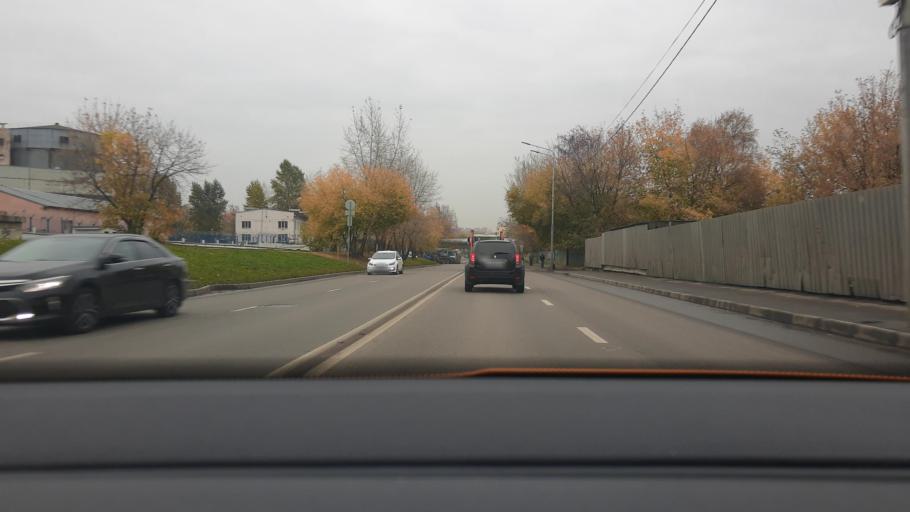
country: RU
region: Moscow
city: Metrogorodok
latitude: 55.8198
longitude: 37.7651
